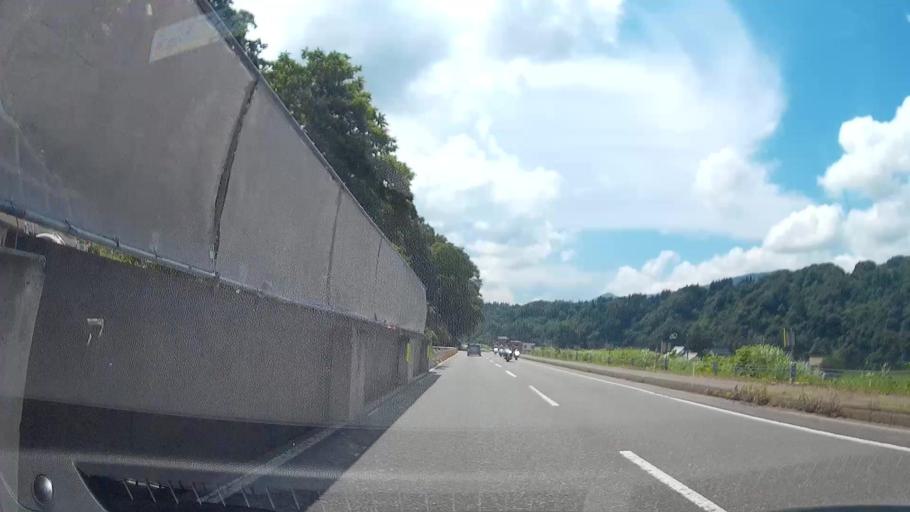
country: JP
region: Niigata
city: Tokamachi
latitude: 36.9999
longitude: 138.6225
